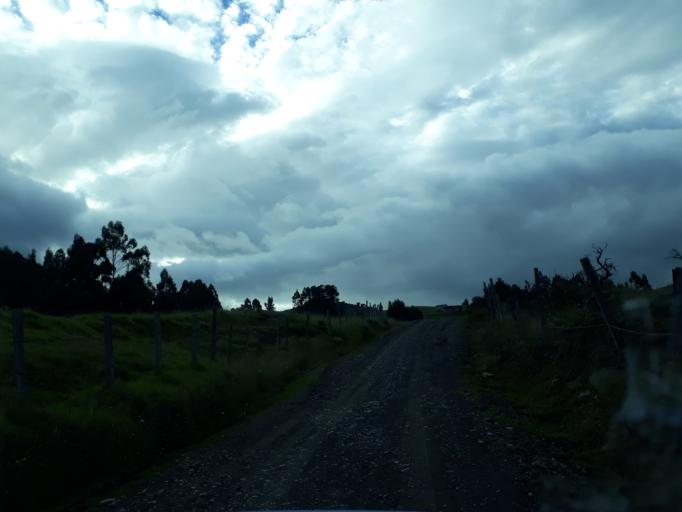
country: CO
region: Cundinamarca
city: Carmen de Carupa
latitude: 5.3105
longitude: -73.9100
